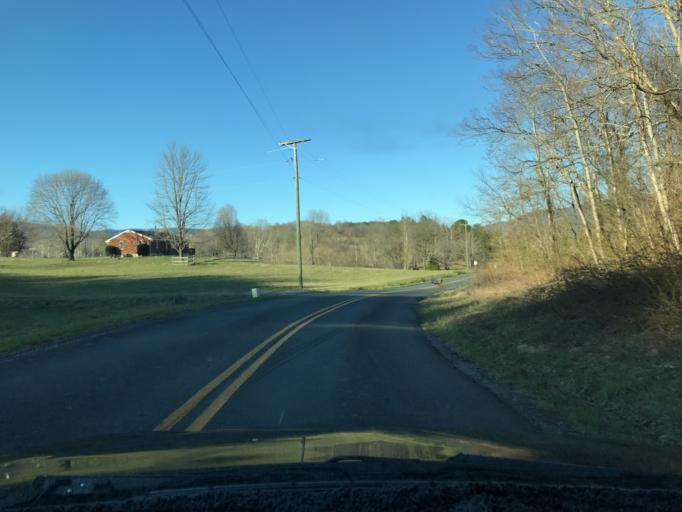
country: US
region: Virginia
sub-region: Botetourt County
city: Blue Ridge
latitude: 37.4138
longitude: -79.7020
